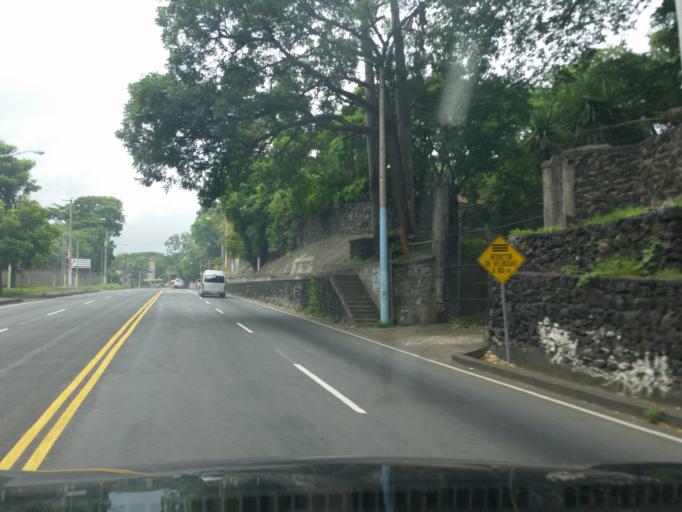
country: NI
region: Managua
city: El Crucero
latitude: 12.0713
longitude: -86.3241
